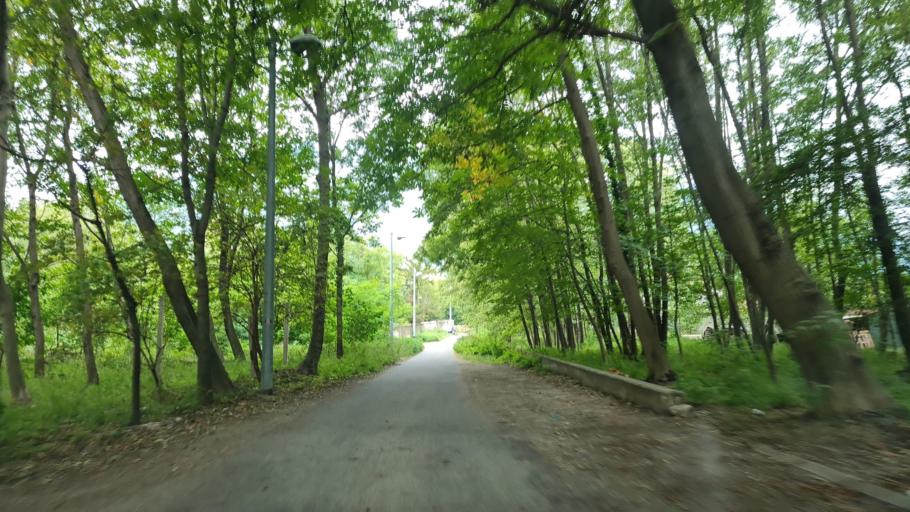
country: IT
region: Piedmont
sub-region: Provincia di Torino
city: Borgofranco d'Ivrea
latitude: 45.5132
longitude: 7.8664
